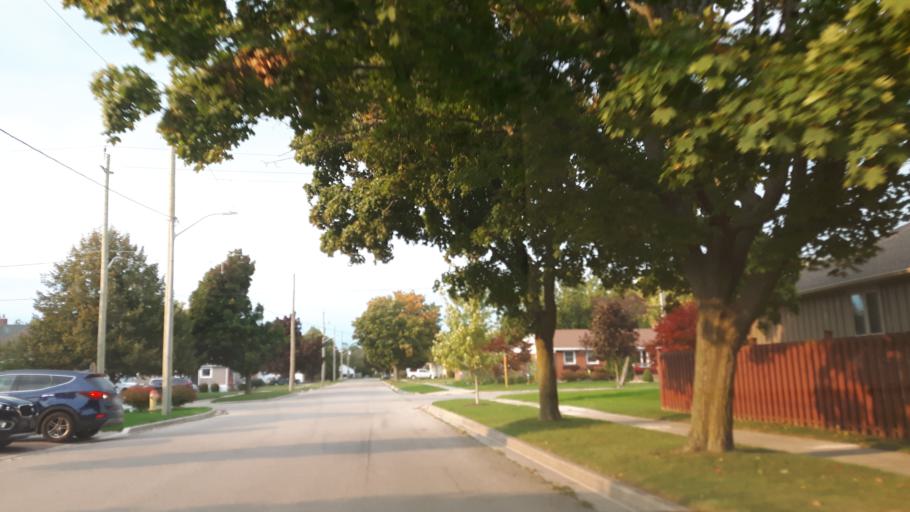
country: CA
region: Ontario
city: Goderich
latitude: 43.7369
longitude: -81.7203
